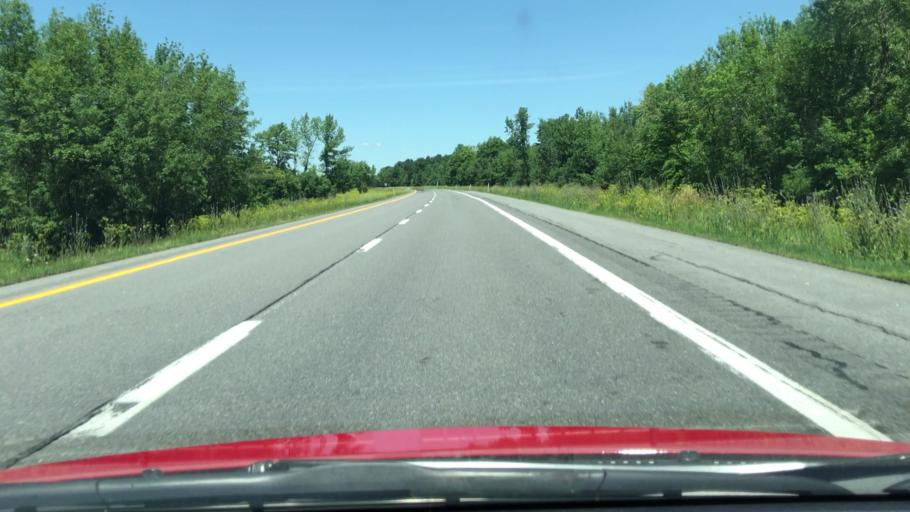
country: US
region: New York
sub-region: Clinton County
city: Champlain
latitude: 44.9197
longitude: -73.4462
